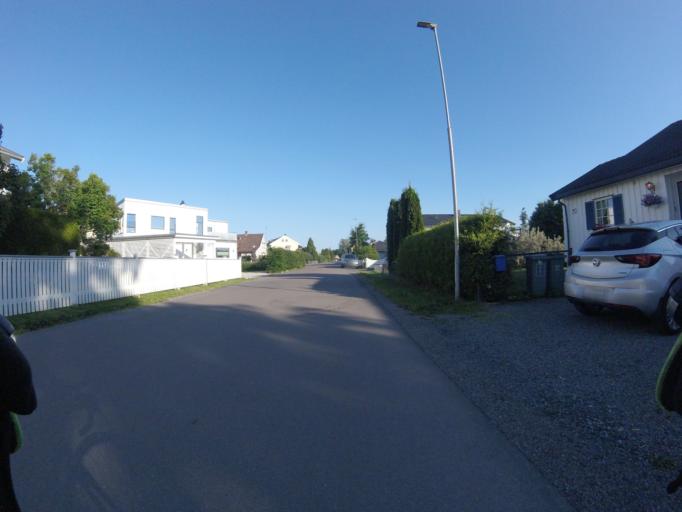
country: NO
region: Akershus
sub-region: Skedsmo
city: Lillestrom
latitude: 59.9627
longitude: 11.0380
